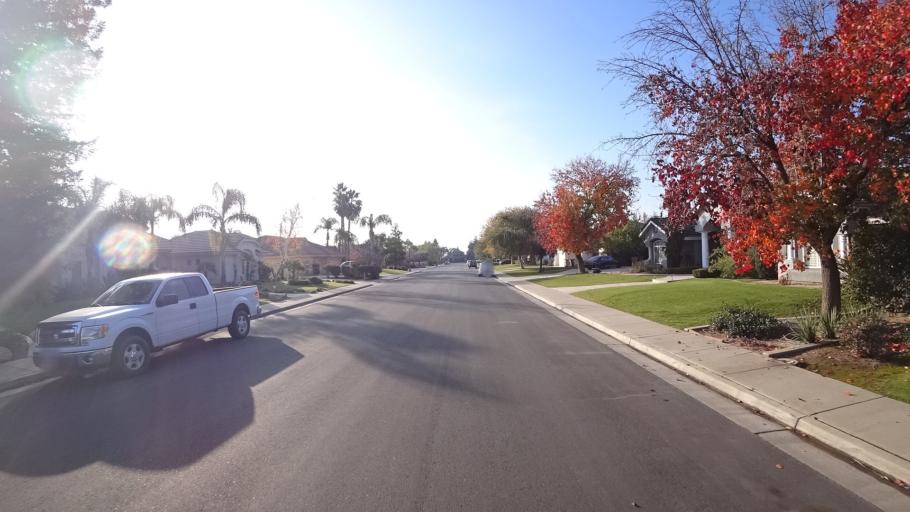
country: US
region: California
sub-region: Kern County
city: Rosedale
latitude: 35.3718
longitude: -119.1376
